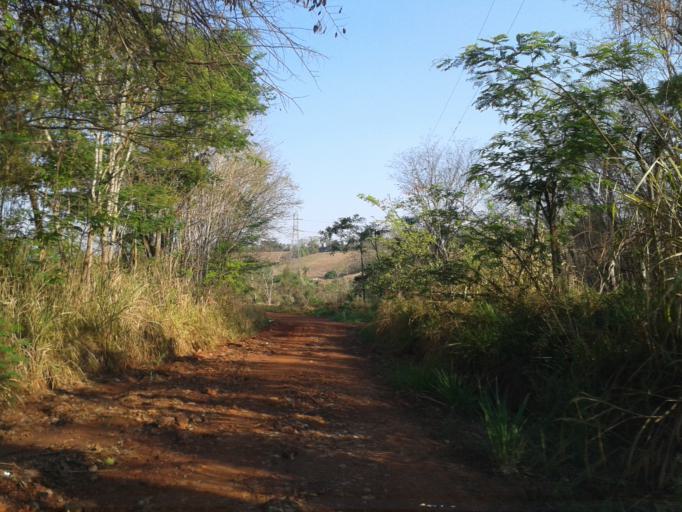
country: BR
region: Minas Gerais
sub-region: Ituiutaba
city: Ituiutaba
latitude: -18.9449
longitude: -49.4608
